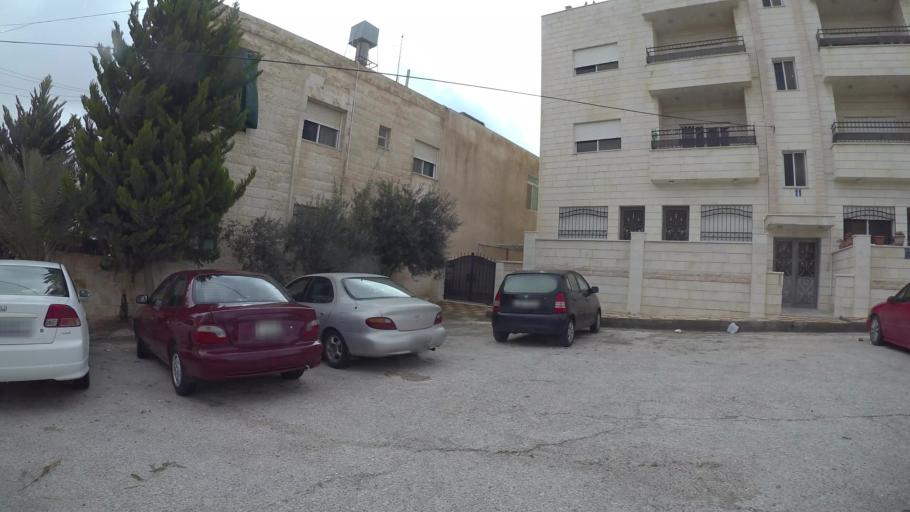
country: JO
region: Amman
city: Al Jubayhah
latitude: 32.0659
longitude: 35.8786
